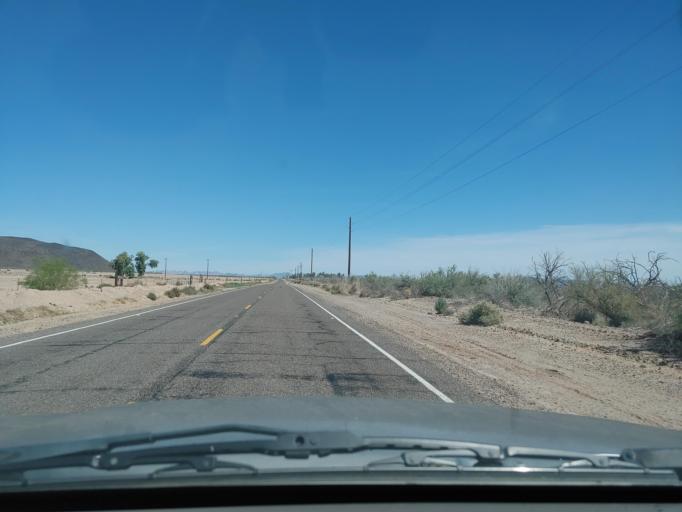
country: US
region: Arizona
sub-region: Maricopa County
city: Gila Bend
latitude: 32.9765
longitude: -113.3059
